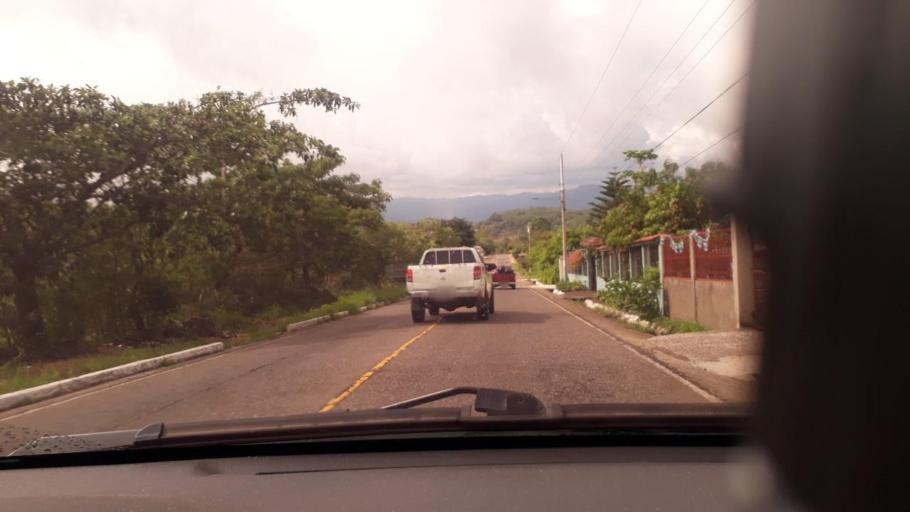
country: GT
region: Jutiapa
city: Quesada
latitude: 14.2065
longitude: -90.0245
